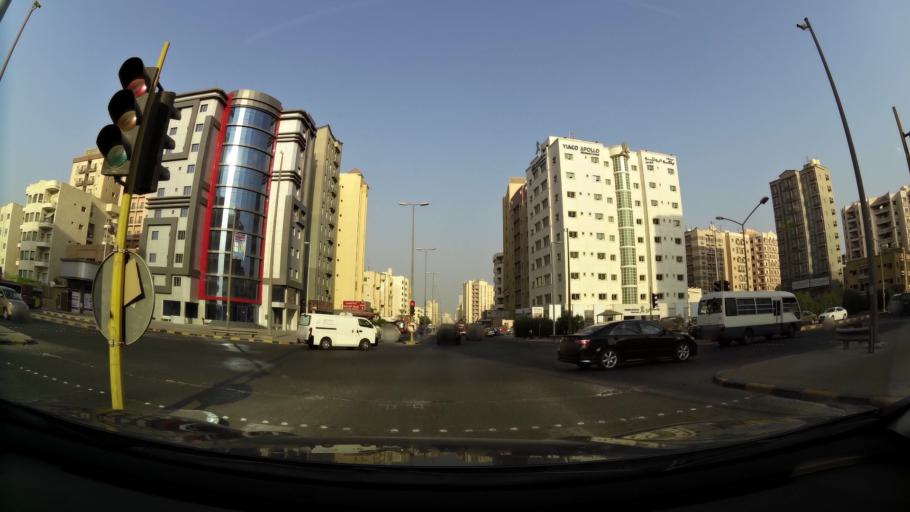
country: KW
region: Muhafazat Hawalli
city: As Salimiyah
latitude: 29.3306
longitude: 48.0543
